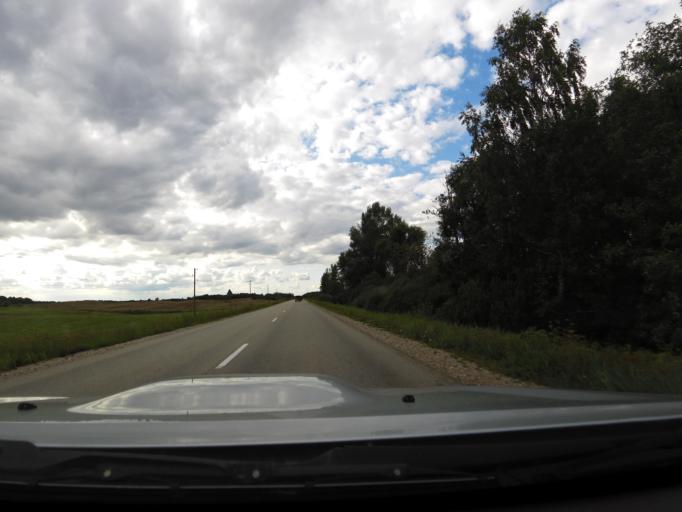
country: LV
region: Akniste
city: Akniste
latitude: 55.9867
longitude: 25.9857
